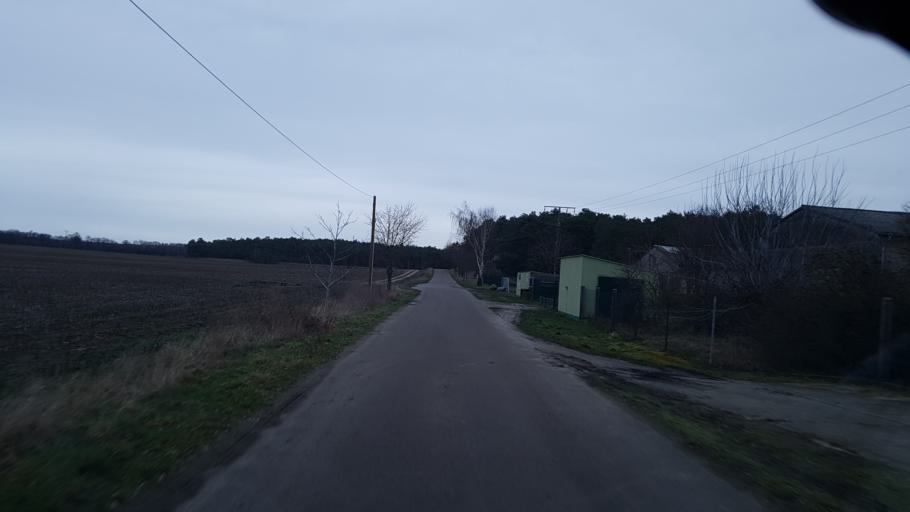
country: DE
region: Brandenburg
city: Schlieben
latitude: 51.7130
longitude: 13.3089
